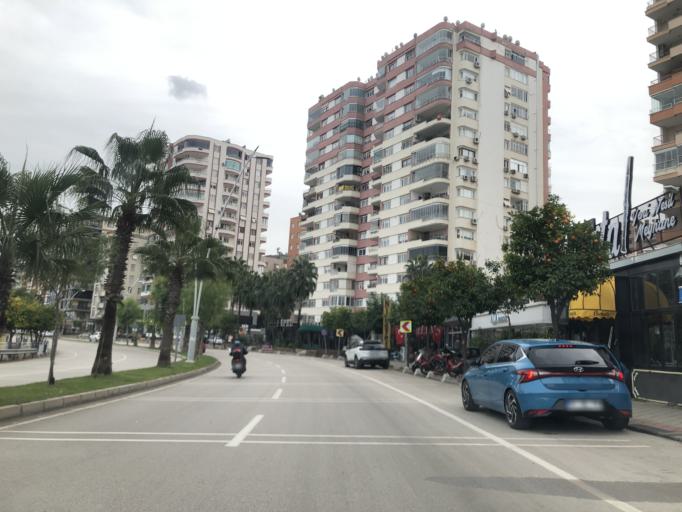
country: TR
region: Adana
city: Adana
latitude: 37.0524
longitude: 35.2923
